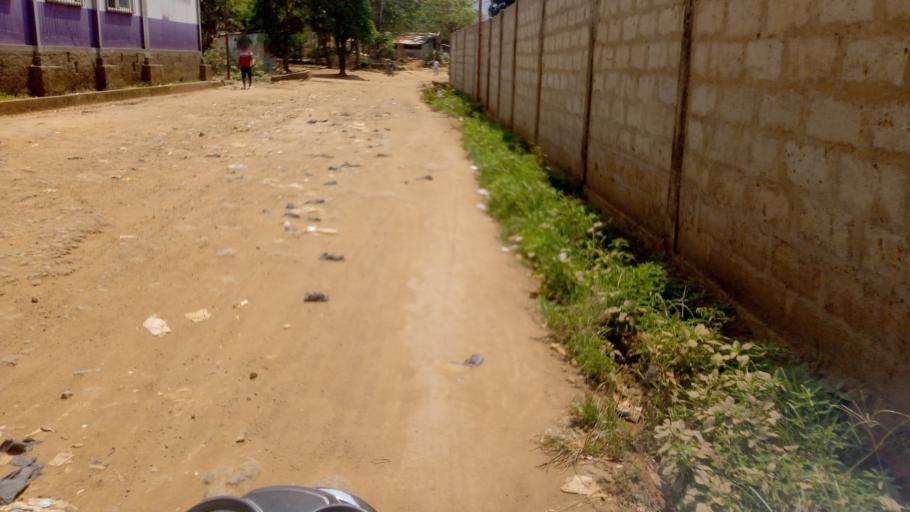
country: SL
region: Western Area
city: Waterloo
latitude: 8.3260
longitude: -13.0740
